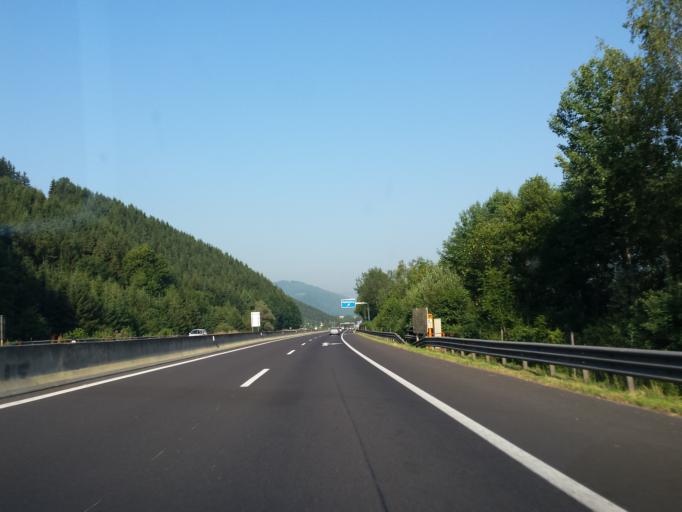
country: AT
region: Styria
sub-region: Politischer Bezirk Bruck-Muerzzuschlag
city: Frauenberg
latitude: 47.4490
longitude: 15.3339
